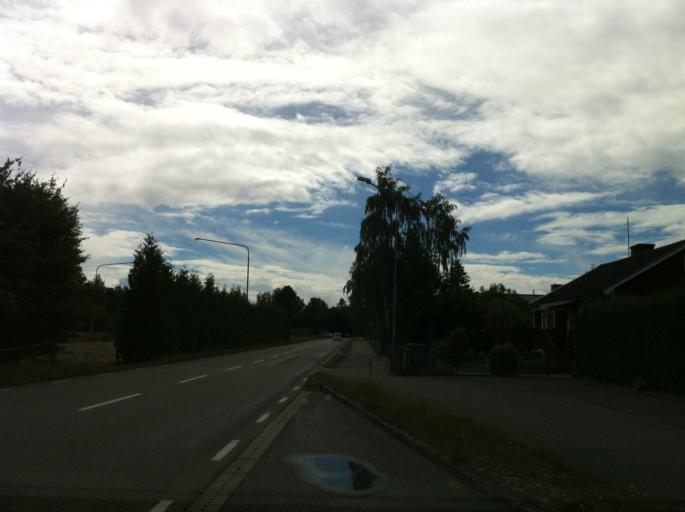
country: SE
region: Skane
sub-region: Hassleholms Kommun
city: Tormestorp
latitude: 56.1801
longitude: 13.6808
